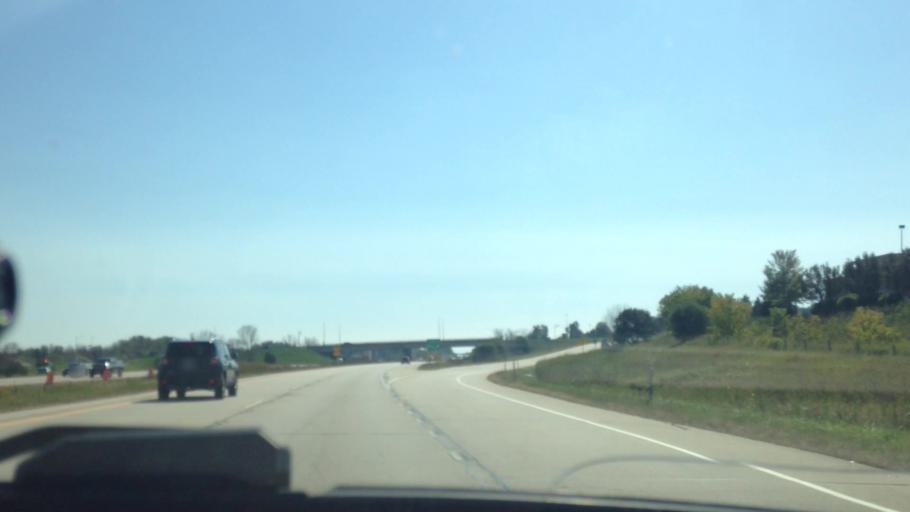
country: US
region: Wisconsin
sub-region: Ozaukee County
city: Grafton
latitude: 43.3240
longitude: -87.9197
